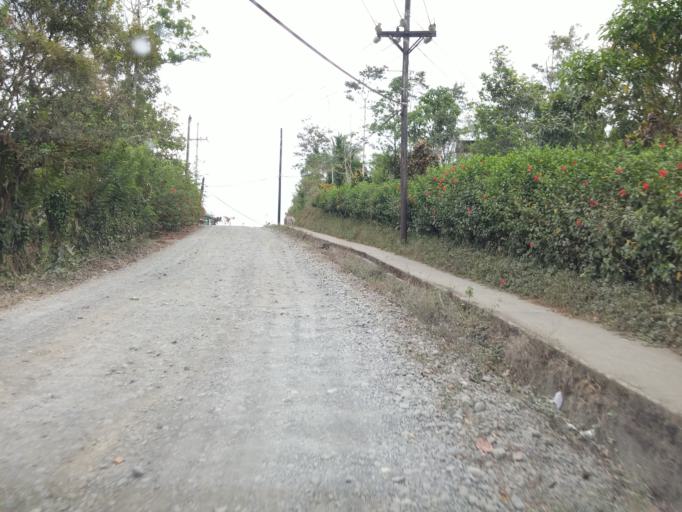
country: CR
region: Alajuela
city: Quesada
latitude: 10.3186
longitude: -84.5185
